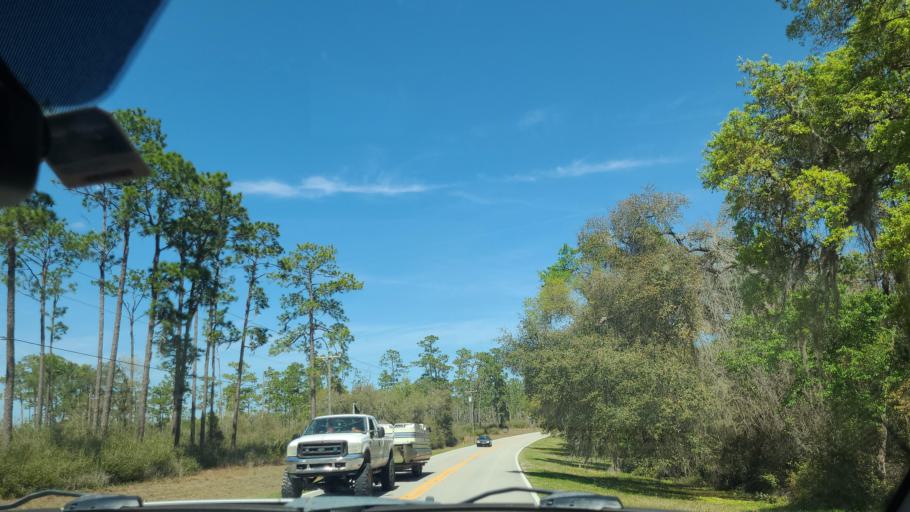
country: US
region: Florida
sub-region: Putnam County
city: Interlachen
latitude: 29.3722
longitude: -81.8030
